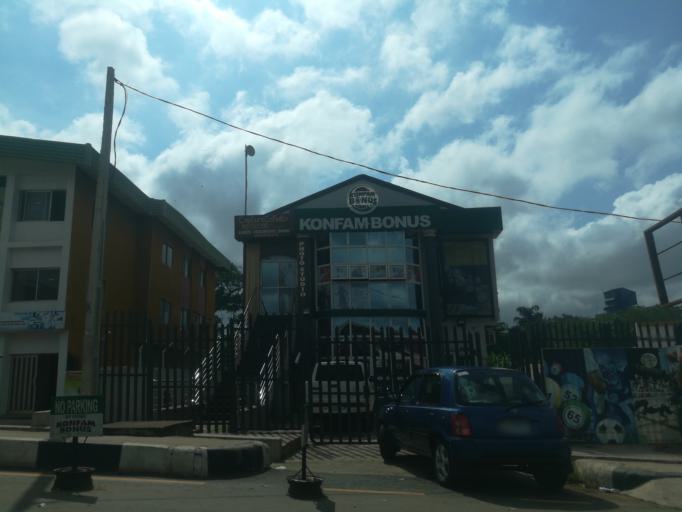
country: NG
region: Oyo
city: Ibadan
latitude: 7.3449
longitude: 3.8765
